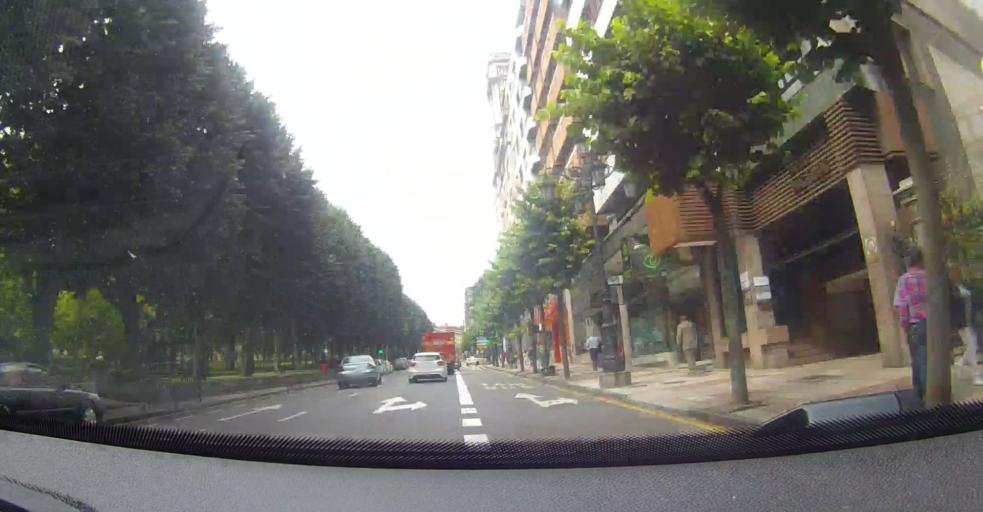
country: ES
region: Asturias
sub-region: Province of Asturias
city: Oviedo
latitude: 43.3629
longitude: -5.8512
